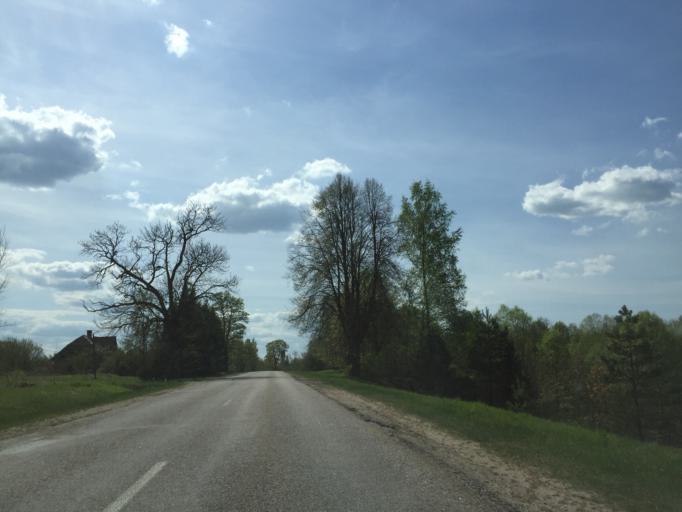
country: LV
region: Limbazu Rajons
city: Limbazi
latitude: 57.3513
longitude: 24.6653
